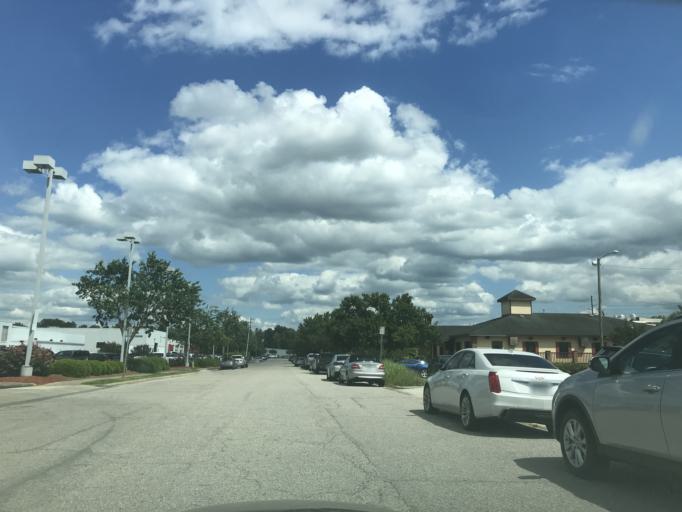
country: US
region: North Carolina
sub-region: Wake County
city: Raleigh
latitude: 35.8168
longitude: -78.6245
